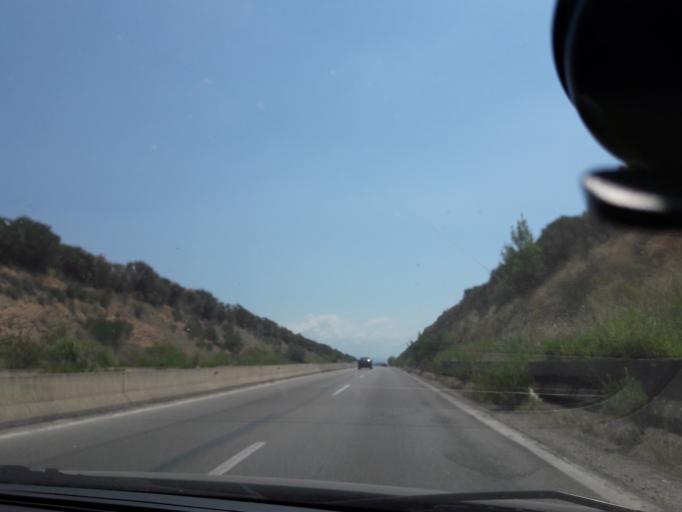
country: GR
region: Central Macedonia
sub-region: Nomos Chalkidikis
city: Nea Triglia
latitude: 40.2977
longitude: 23.1378
